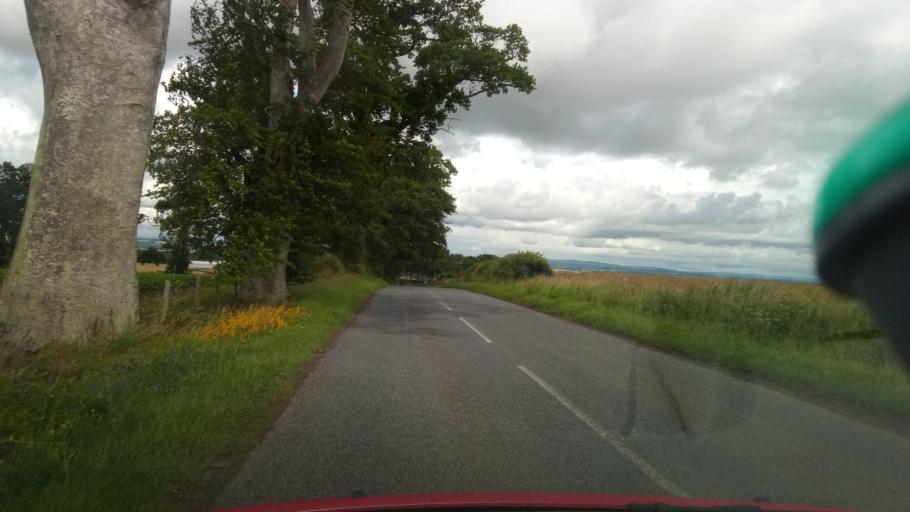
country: GB
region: Scotland
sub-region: The Scottish Borders
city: Kelso
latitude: 55.5703
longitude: -2.4196
